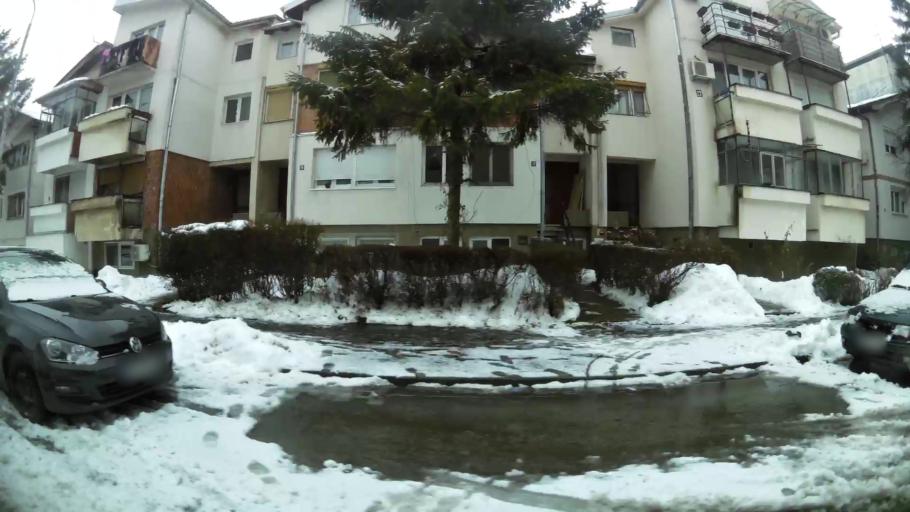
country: RS
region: Central Serbia
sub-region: Belgrade
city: Zemun
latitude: 44.8727
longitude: 20.3197
